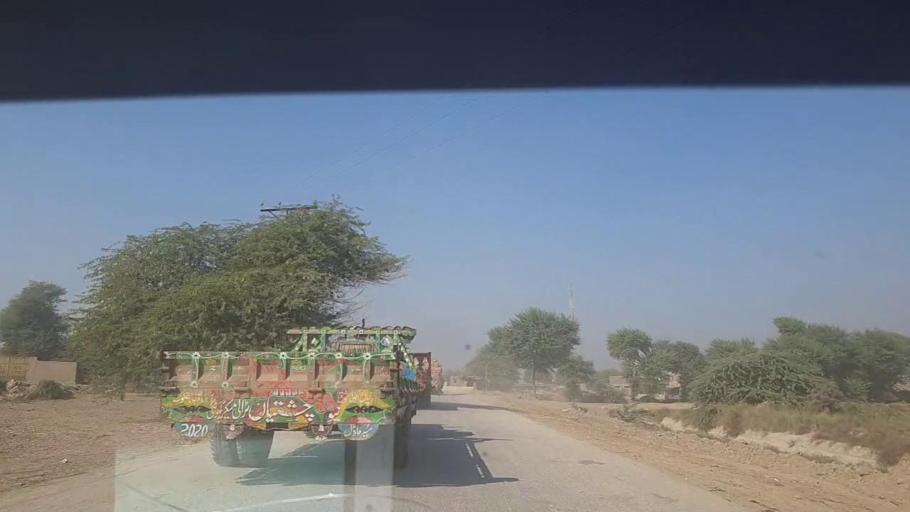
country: PK
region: Sindh
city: Kot Diji
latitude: 27.4382
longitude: 68.6344
